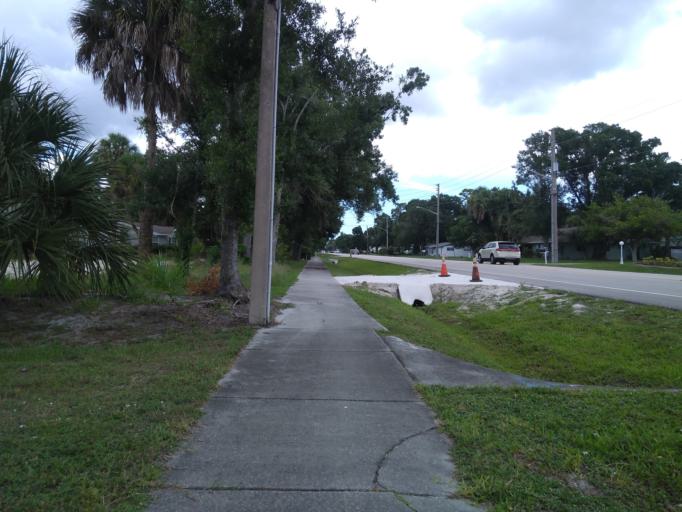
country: US
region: Florida
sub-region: Indian River County
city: Vero Beach South
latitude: 27.6336
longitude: -80.4139
